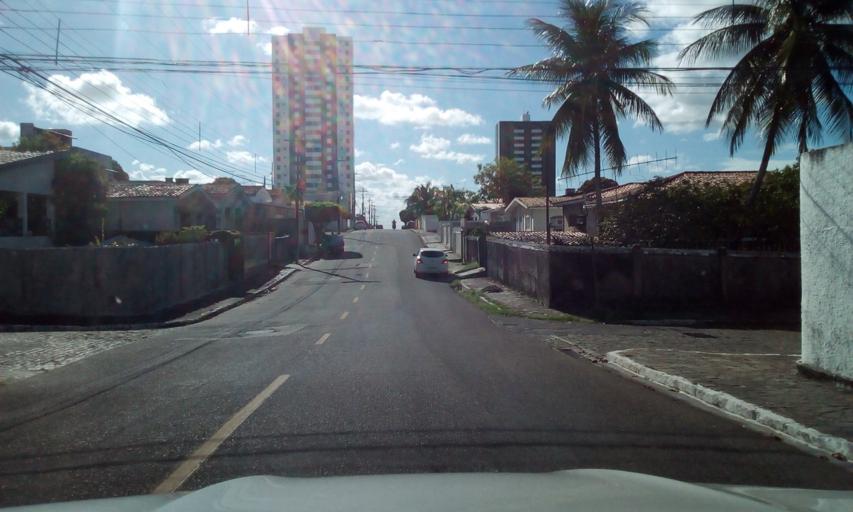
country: BR
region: Paraiba
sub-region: Joao Pessoa
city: Joao Pessoa
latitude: -7.1102
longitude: -34.8639
